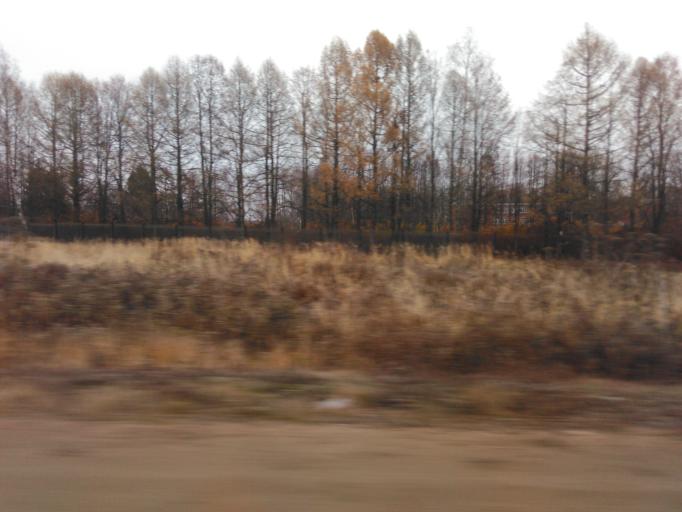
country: RU
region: Moskovskaya
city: Ashukino
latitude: 56.1702
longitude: 37.9401
